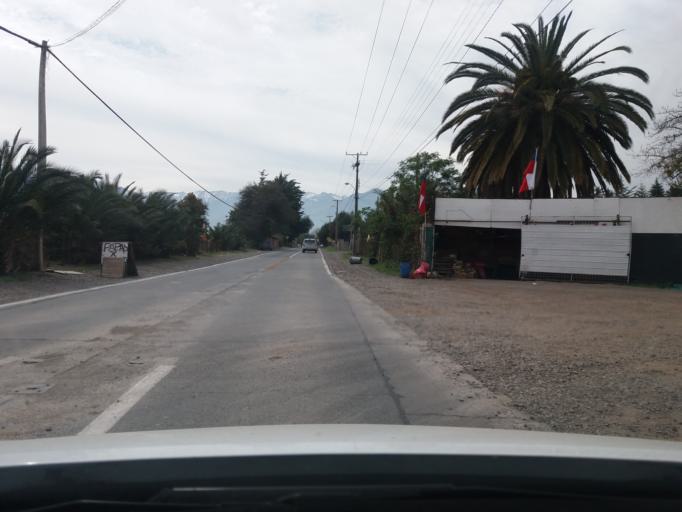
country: CL
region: Valparaiso
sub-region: Provincia de Los Andes
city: Los Andes
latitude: -32.8334
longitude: -70.6286
